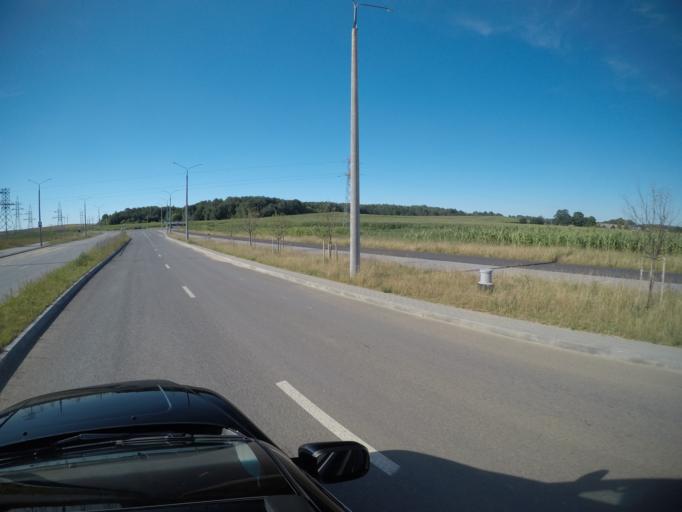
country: BY
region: Grodnenskaya
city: Hrodna
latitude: 53.7219
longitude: 23.8683
